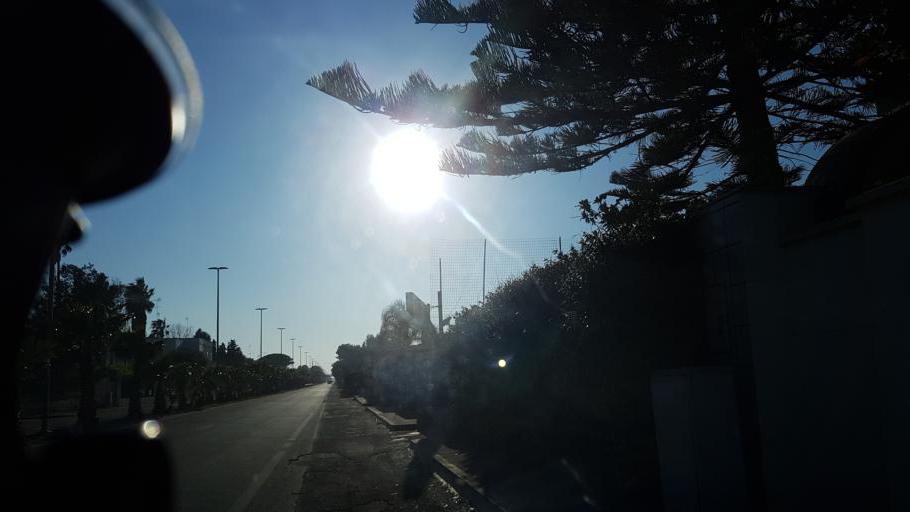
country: IT
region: Apulia
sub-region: Provincia di Lecce
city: Struda
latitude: 40.3894
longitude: 18.3030
